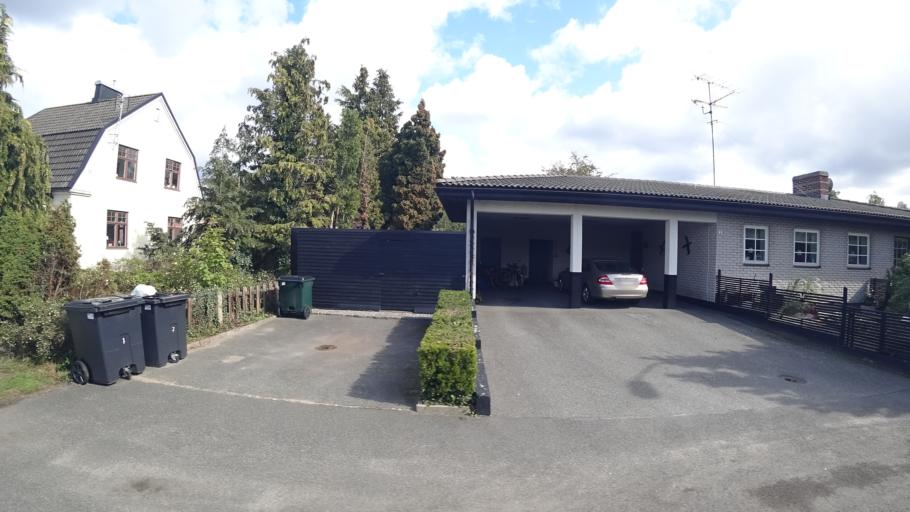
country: SE
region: Skane
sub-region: Kristianstads Kommun
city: Ahus
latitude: 55.9318
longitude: 14.3092
